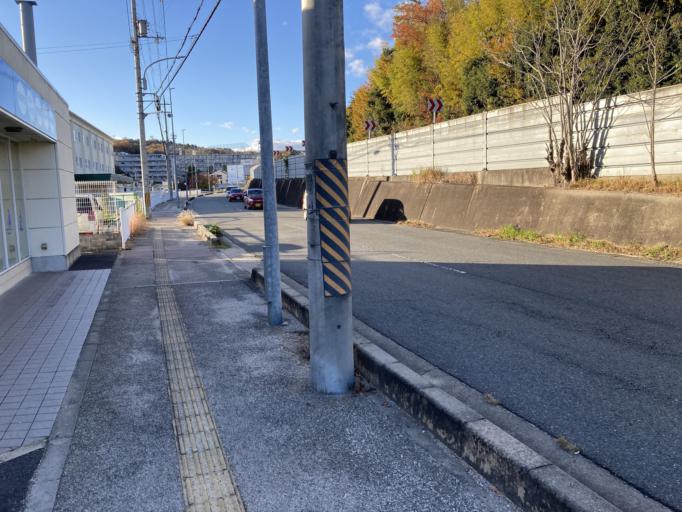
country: JP
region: Nara
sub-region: Ikoma-shi
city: Ikoma
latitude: 34.6856
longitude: 135.7320
